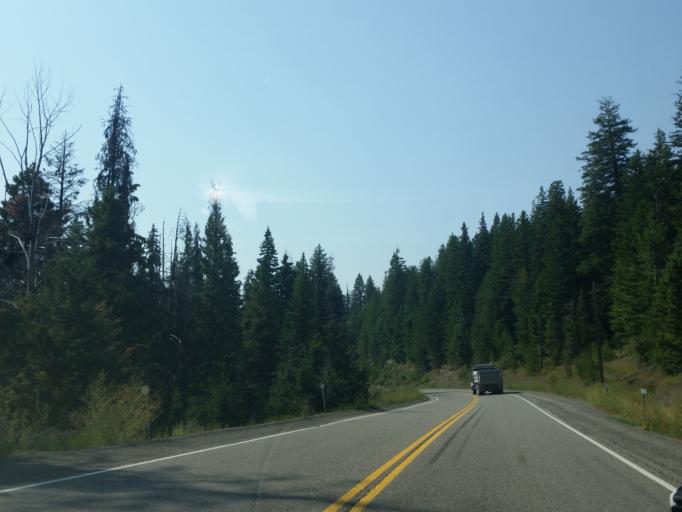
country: CA
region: British Columbia
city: Princeton
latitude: 49.2230
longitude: -120.5464
